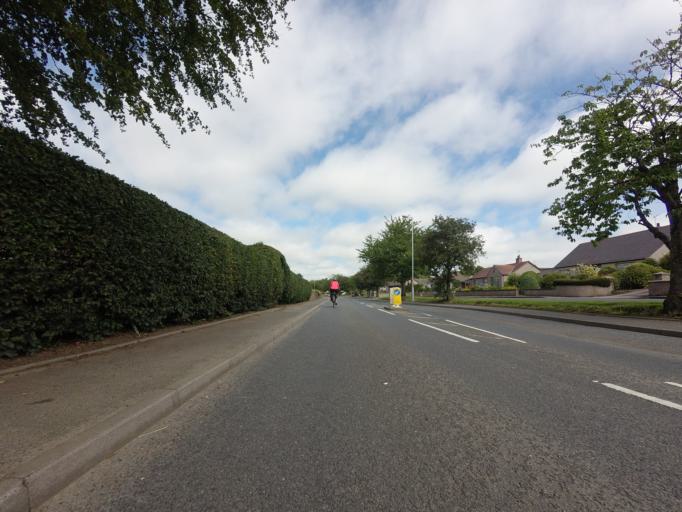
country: GB
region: Scotland
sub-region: Aberdeenshire
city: Turriff
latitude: 57.5408
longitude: -2.4714
